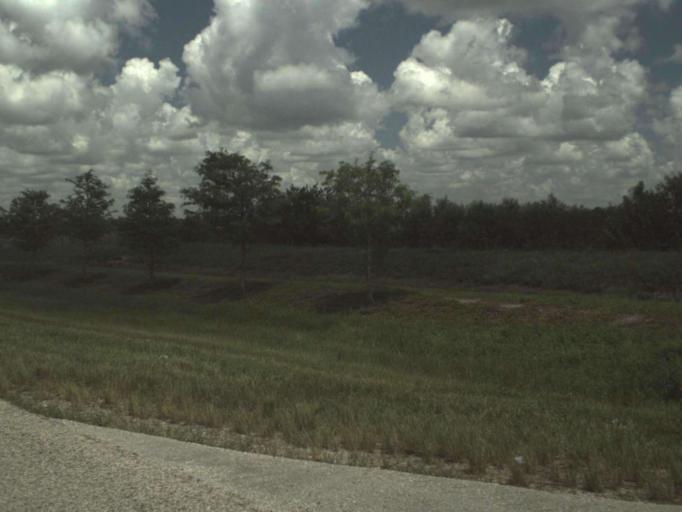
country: US
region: Florida
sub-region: Indian River County
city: Fellsmere
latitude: 27.6420
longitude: -80.7626
